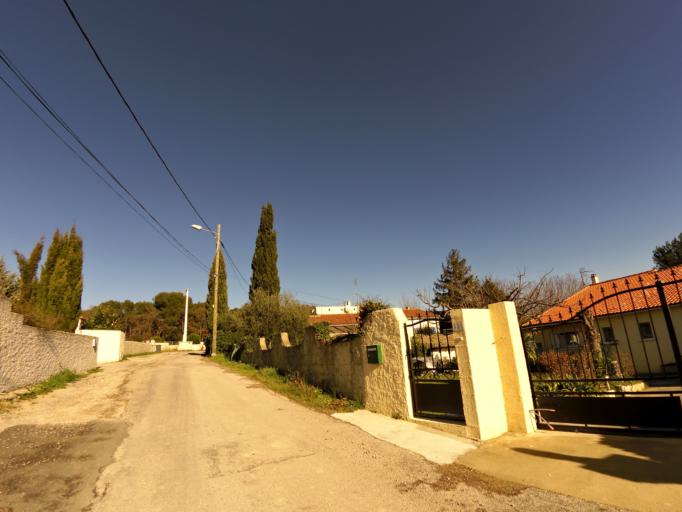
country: FR
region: Languedoc-Roussillon
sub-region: Departement du Gard
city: Aigues-Vives
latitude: 43.7301
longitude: 4.1859
